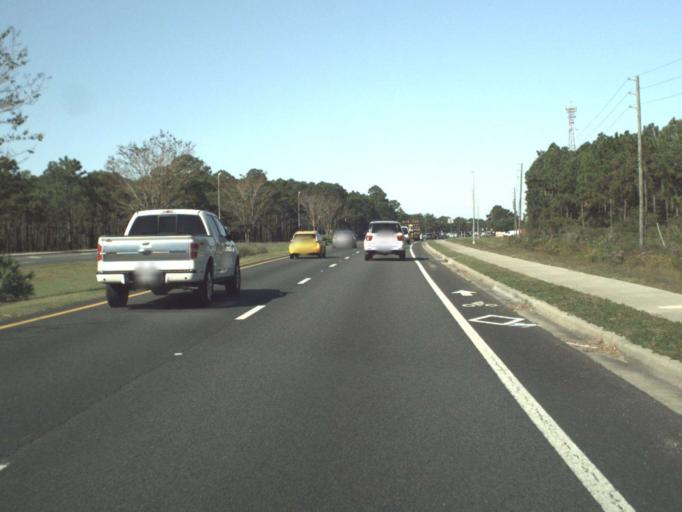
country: US
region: Florida
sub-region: Walton County
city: Miramar Beach
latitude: 30.3760
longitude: -86.3012
